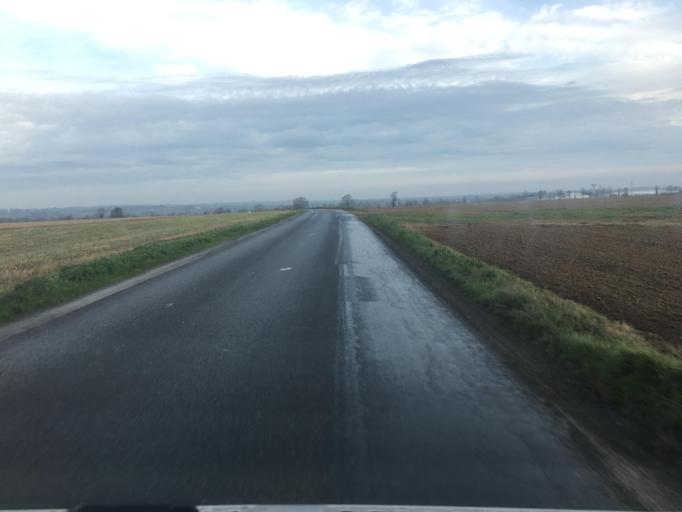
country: FR
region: Lower Normandy
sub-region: Departement du Calvados
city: Creully
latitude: 49.2634
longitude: -0.5595
